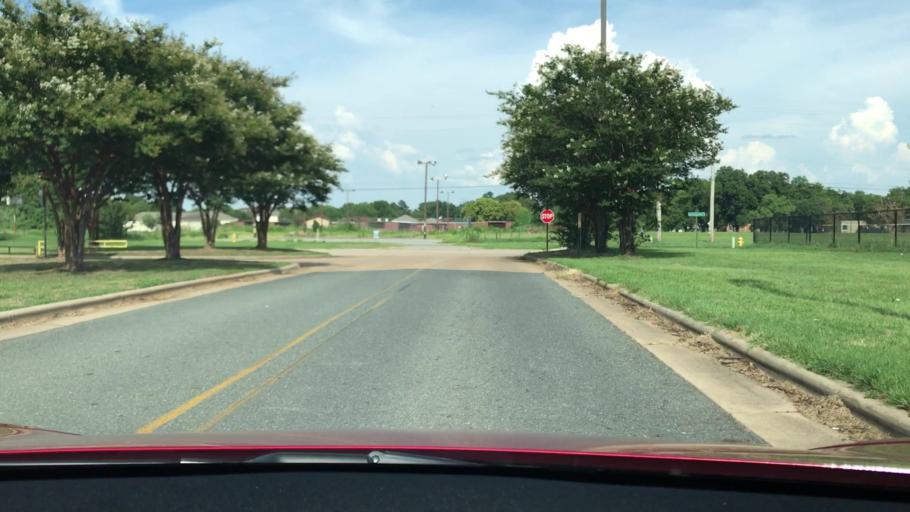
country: US
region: Louisiana
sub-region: Bossier Parish
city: Bossier City
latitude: 32.4623
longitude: -93.6727
